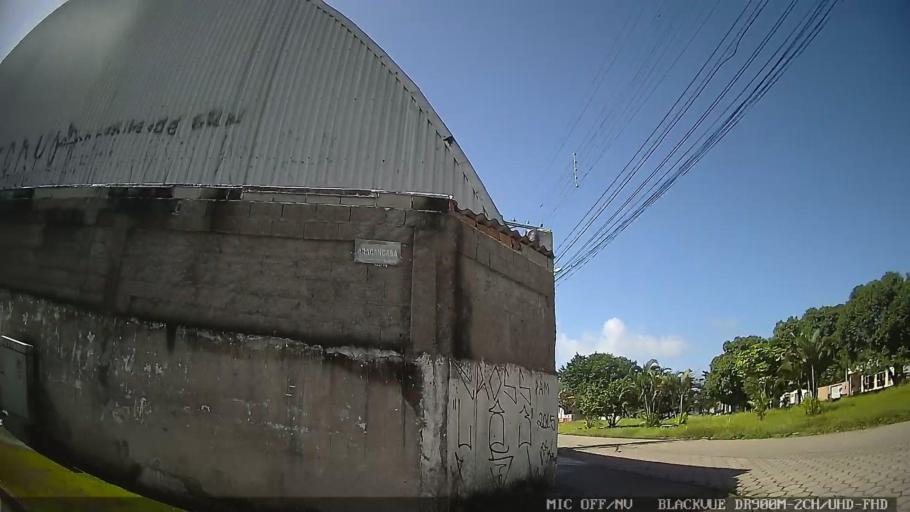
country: BR
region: Sao Paulo
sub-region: Itanhaem
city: Itanhaem
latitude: -24.1637
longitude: -46.7539
